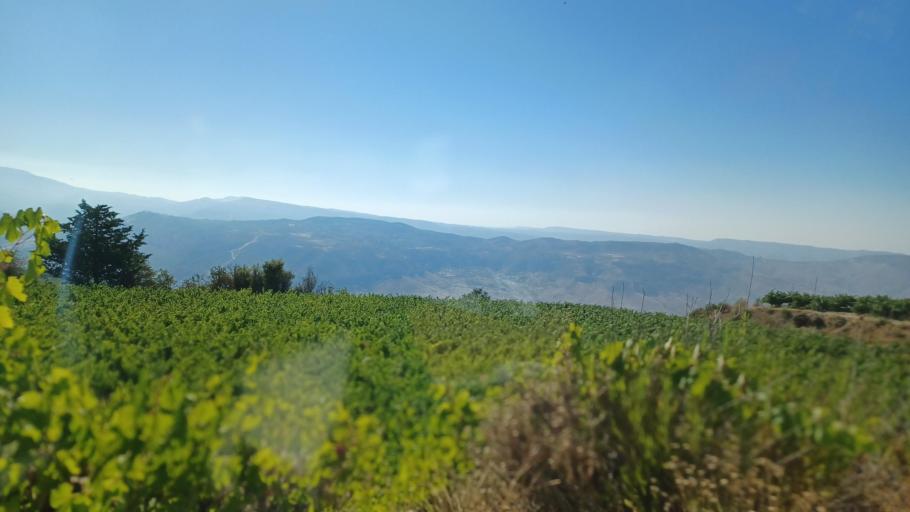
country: CY
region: Pafos
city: Mesogi
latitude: 34.8941
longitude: 32.6268
